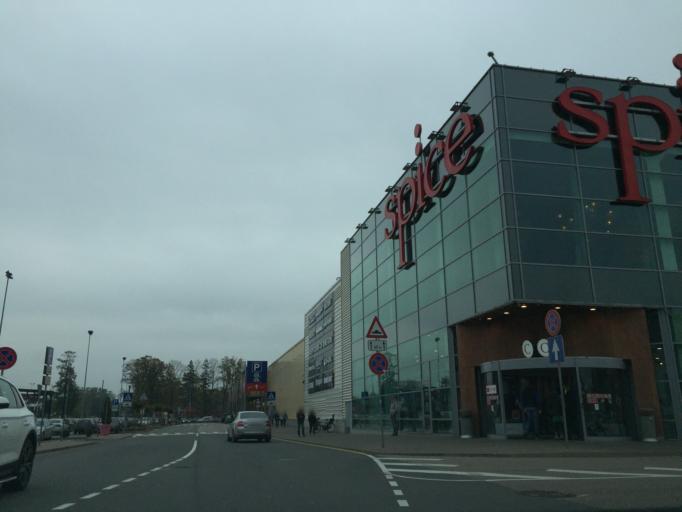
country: LV
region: Marupe
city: Marupe
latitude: 56.9305
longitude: 24.0366
